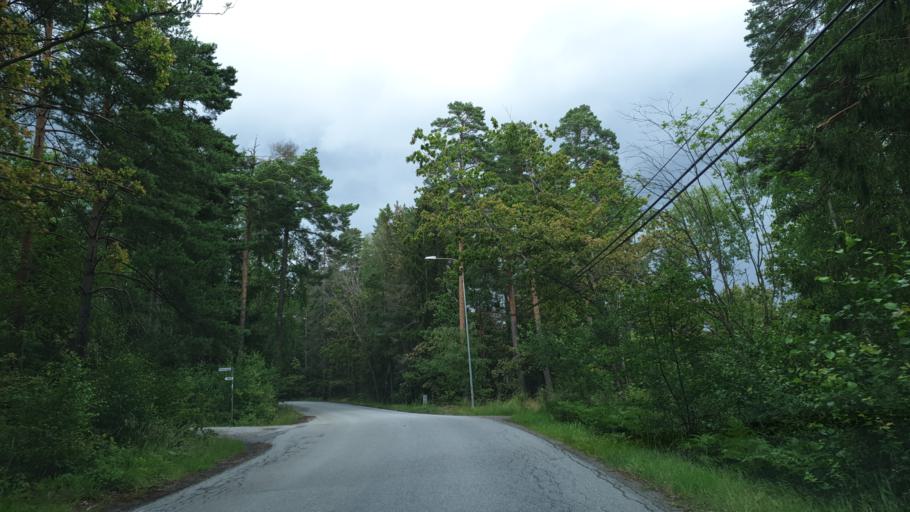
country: SE
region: Stockholm
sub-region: Jarfalla Kommun
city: Jakobsberg
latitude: 59.4261
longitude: 17.8027
